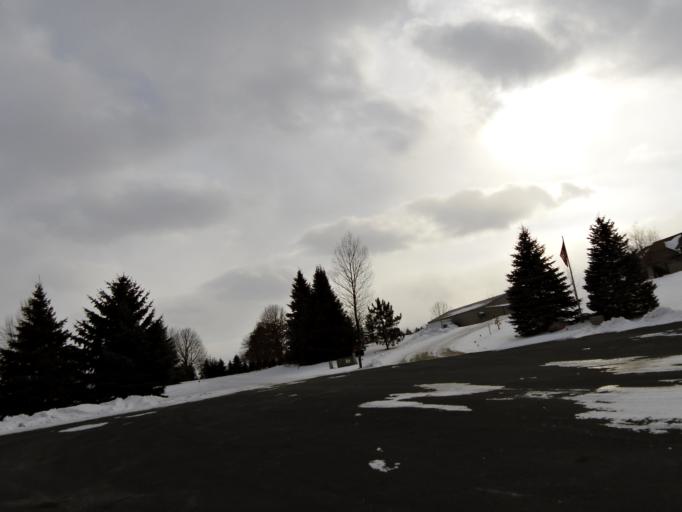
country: US
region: Minnesota
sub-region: Washington County
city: Lake Elmo
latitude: 44.9704
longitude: -92.8497
